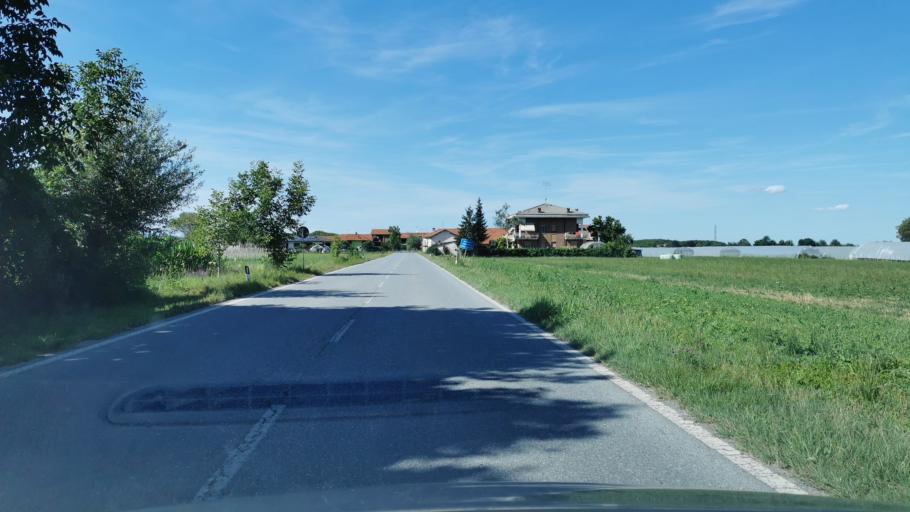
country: IT
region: Piedmont
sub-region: Provincia di Cuneo
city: Boves
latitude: 44.3450
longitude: 7.5578
